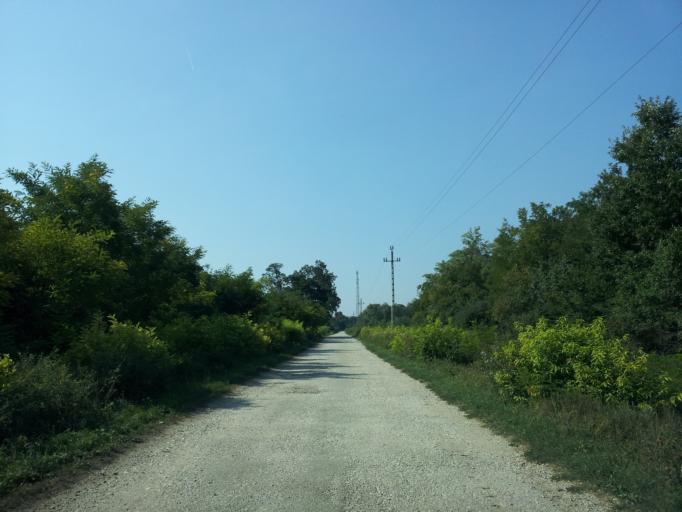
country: HU
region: Fejer
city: Polgardi
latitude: 47.0257
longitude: 18.2795
